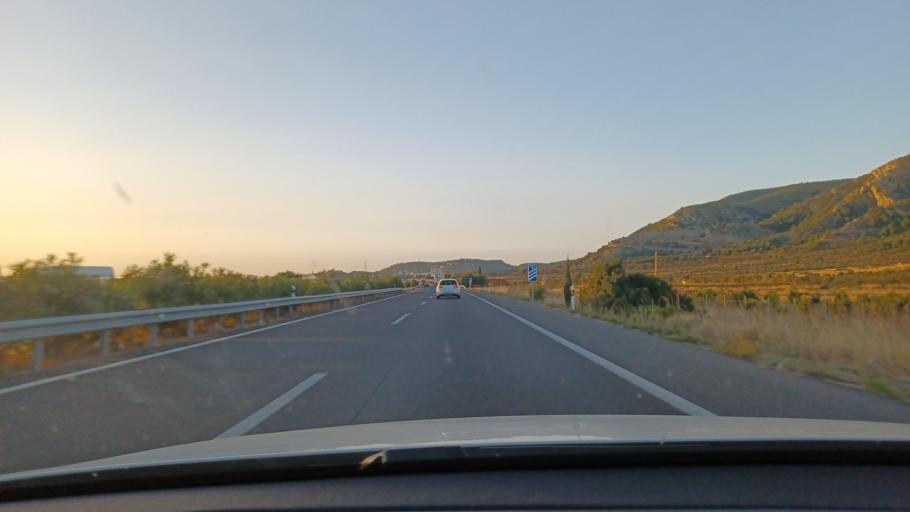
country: ES
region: Valencia
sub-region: Provincia de Castello
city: Orpesa/Oropesa del Mar
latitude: 40.1156
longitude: 0.1312
